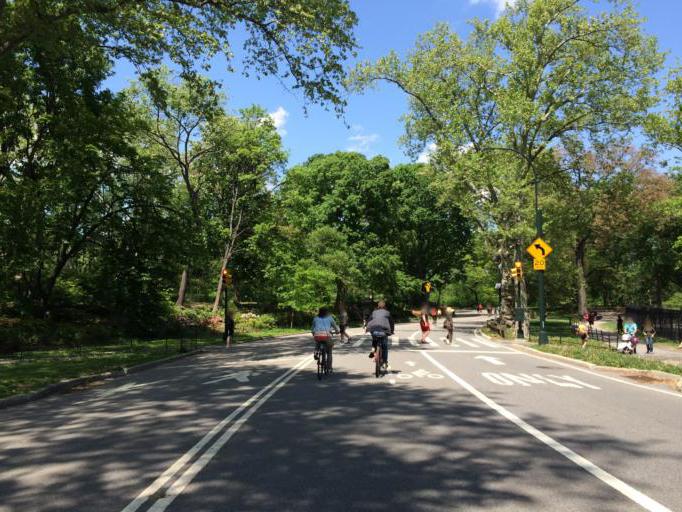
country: US
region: New York
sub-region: New York County
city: Manhattan
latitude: 40.7873
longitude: -73.9570
